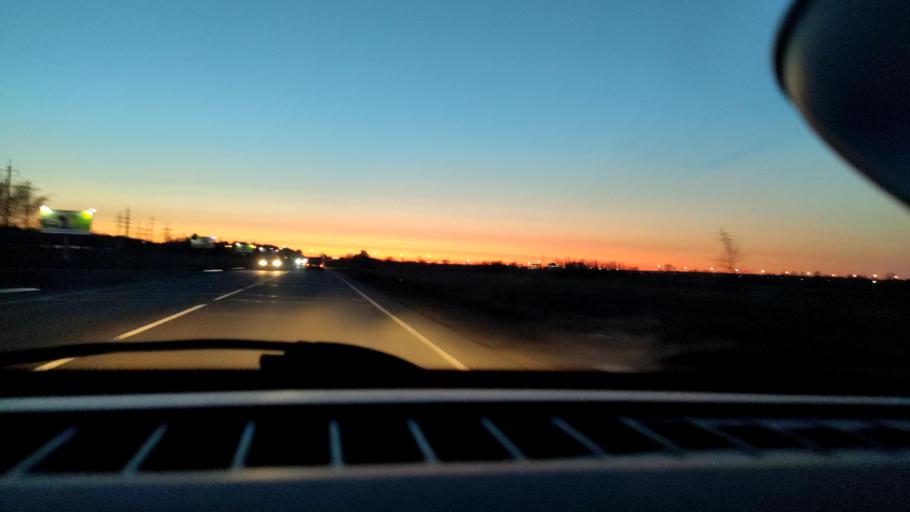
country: RU
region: Samara
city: Samara
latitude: 53.1287
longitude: 50.1589
